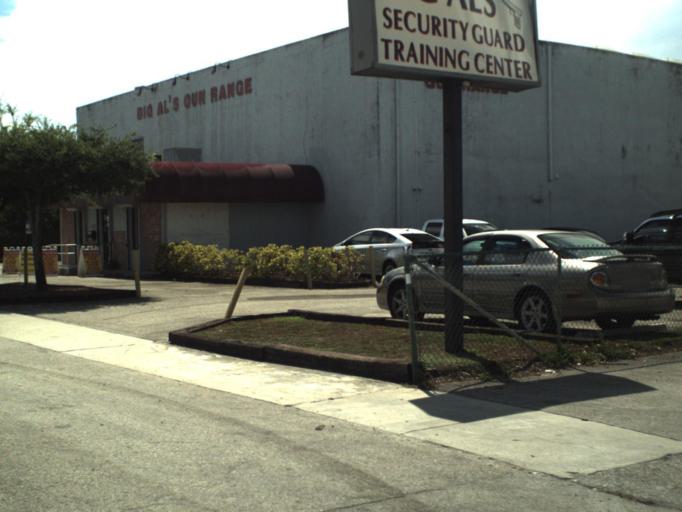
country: US
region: Florida
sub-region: Broward County
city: Pembroke Park
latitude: 25.9846
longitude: -80.1769
